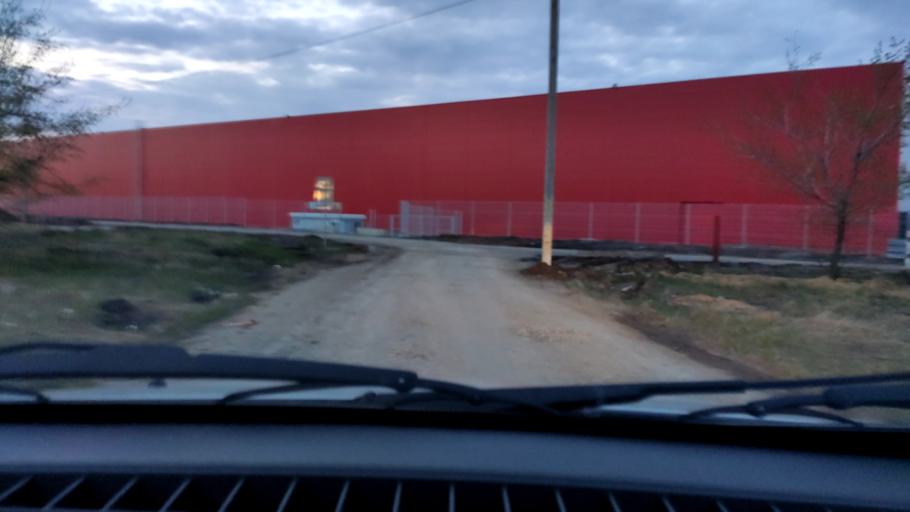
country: RU
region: Voronezj
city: Podgornoye
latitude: 51.7996
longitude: 39.2150
